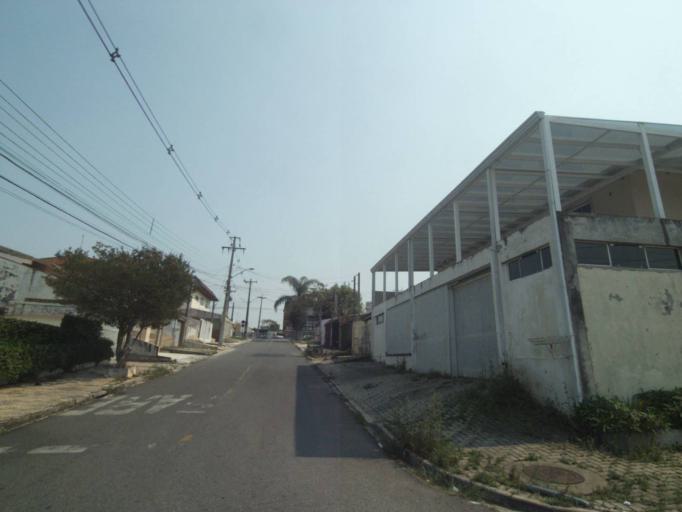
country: BR
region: Parana
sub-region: Sao Jose Dos Pinhais
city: Sao Jose dos Pinhais
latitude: -25.5241
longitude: -49.2434
